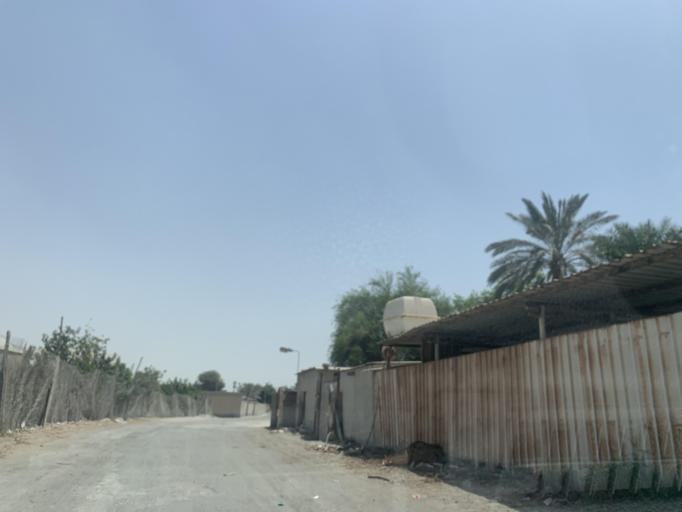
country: BH
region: Central Governorate
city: Madinat Hamad
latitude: 26.1566
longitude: 50.4958
